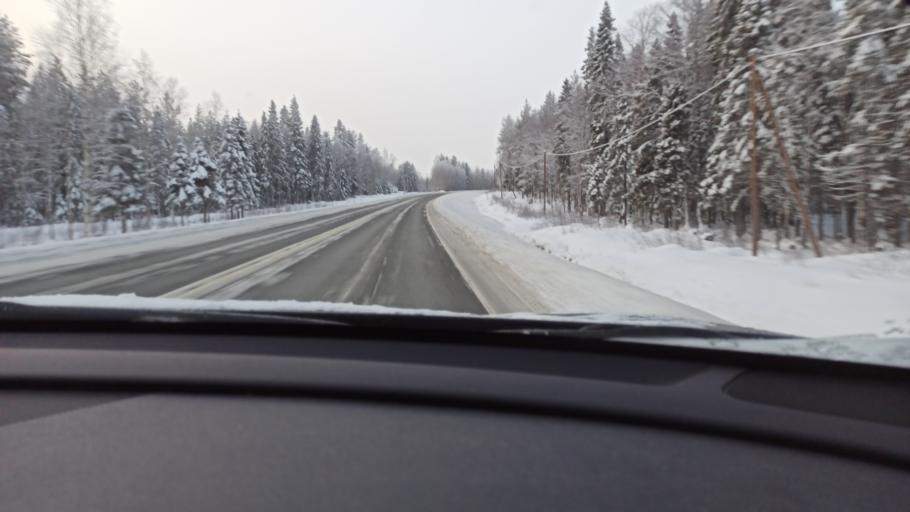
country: FI
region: Lapland
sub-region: Rovaniemi
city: Rovaniemi
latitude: 66.5524
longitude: 25.8957
